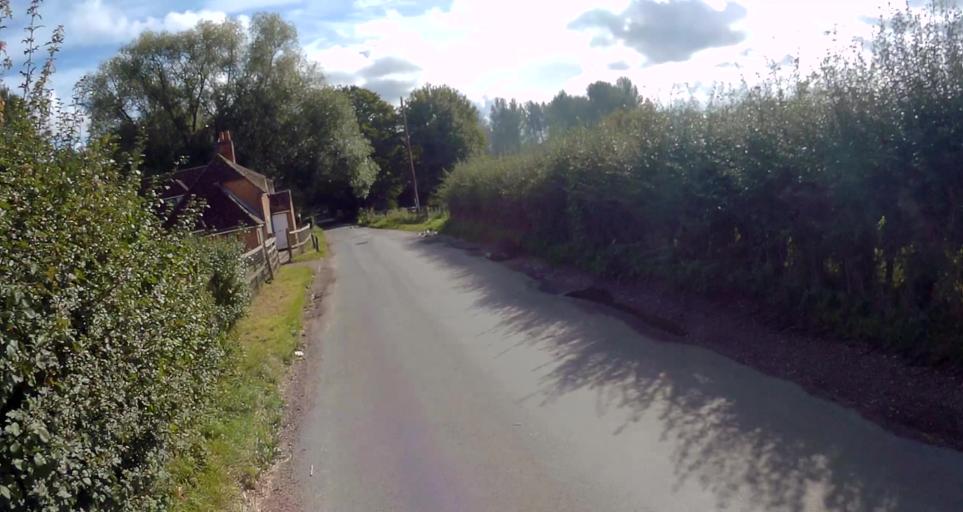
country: GB
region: England
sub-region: Hampshire
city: Kings Worthy
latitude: 51.0902
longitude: -1.2714
